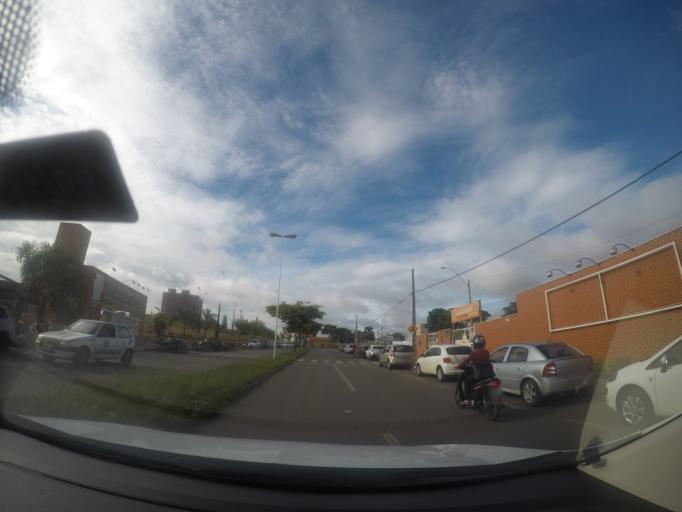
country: BR
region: Goias
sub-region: Goiania
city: Goiania
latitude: -16.6912
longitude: -49.3111
